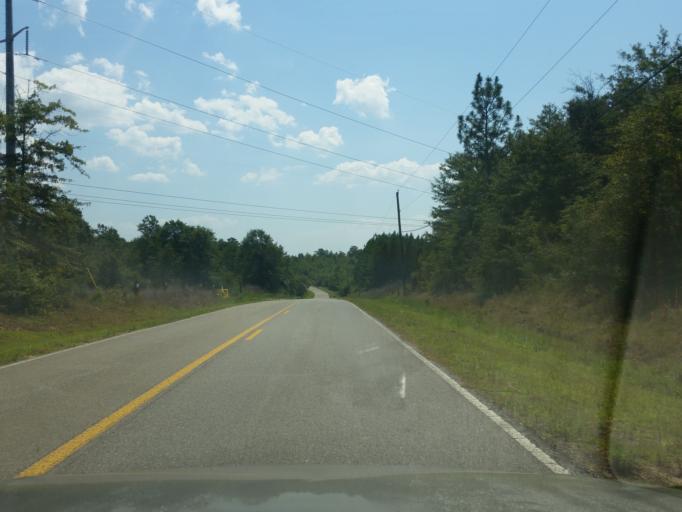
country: US
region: Florida
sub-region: Escambia County
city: Gonzalez
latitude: 30.6188
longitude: -87.2930
